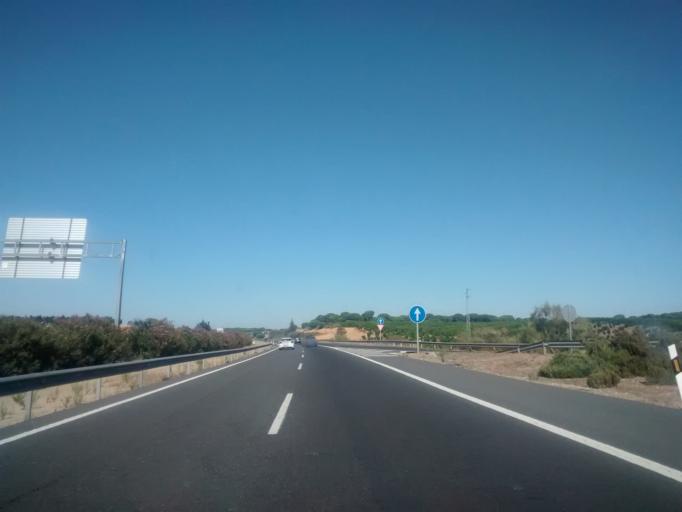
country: ES
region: Andalusia
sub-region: Provincia de Huelva
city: Aljaraque
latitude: 37.3235
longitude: -7.0762
